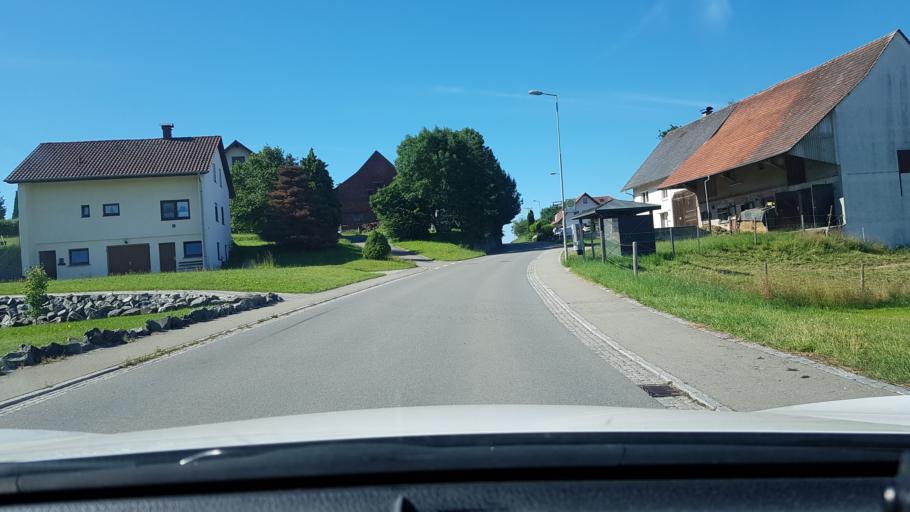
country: DE
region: Baden-Wuerttemberg
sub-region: Tuebingen Region
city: Gutenzell-Hurbel
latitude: 48.0938
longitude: 9.9678
